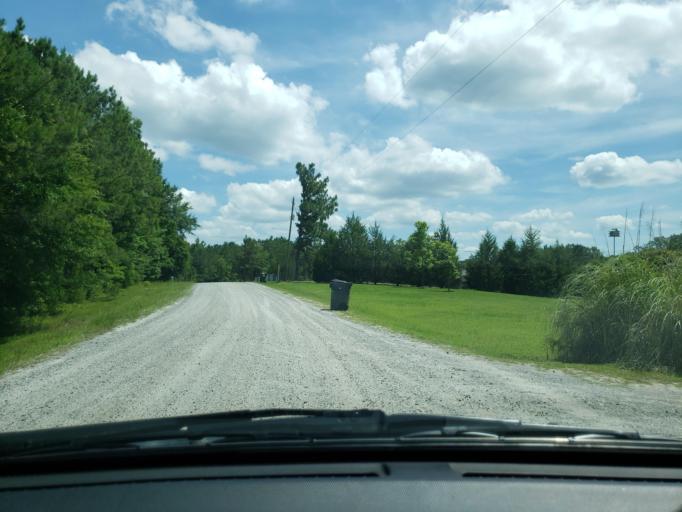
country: US
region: Alabama
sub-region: Elmore County
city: Eclectic
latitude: 32.6247
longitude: -85.9456
